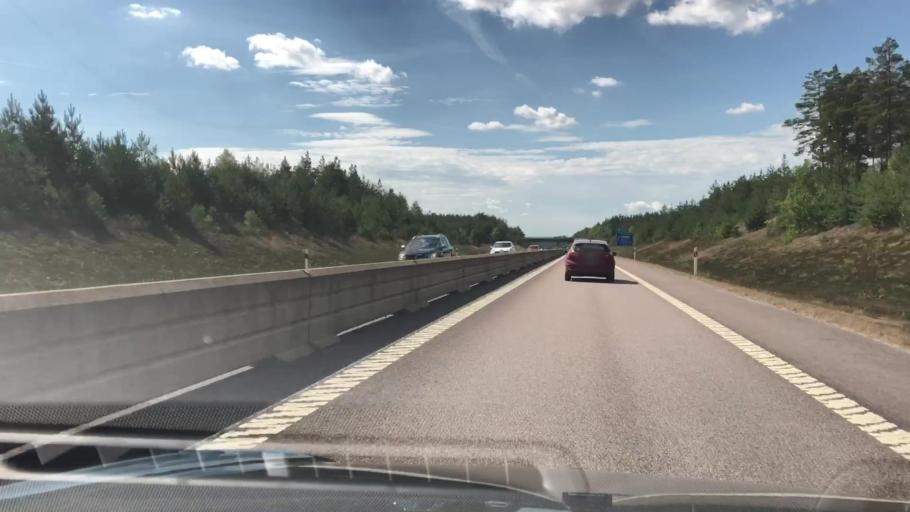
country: SE
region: Kalmar
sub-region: Kalmar Kommun
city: Ljungbyholm
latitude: 56.5974
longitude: 16.1269
